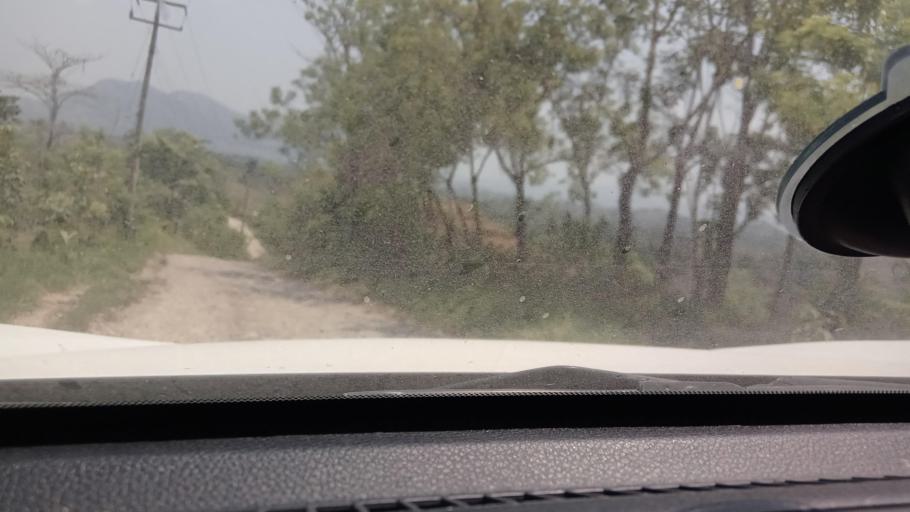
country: MX
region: Tabasco
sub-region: Huimanguillo
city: Francisco Rueda
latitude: 17.4788
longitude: -93.9458
